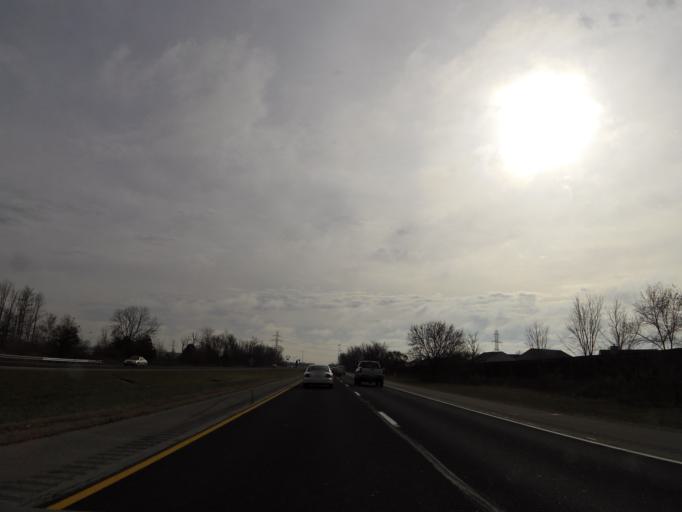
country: US
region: Indiana
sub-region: Marion County
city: Warren Park
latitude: 39.7223
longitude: -86.0166
